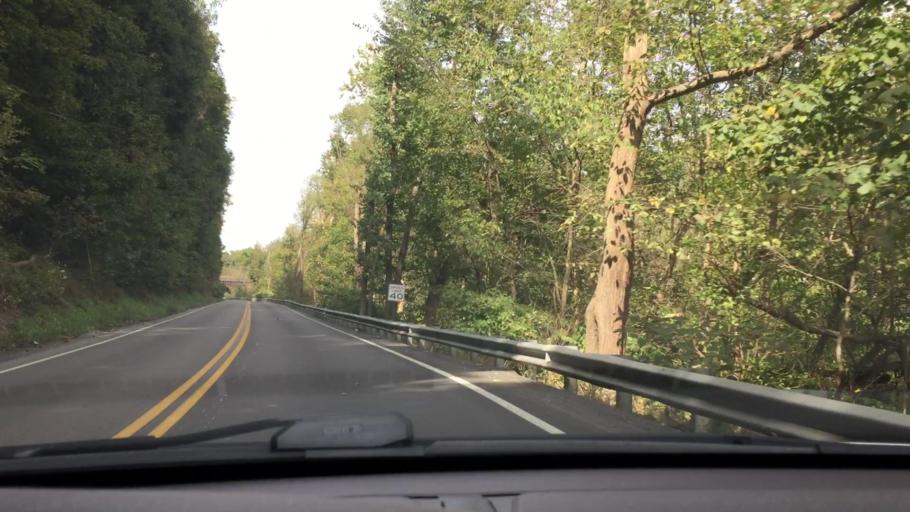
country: US
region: Pennsylvania
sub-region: Washington County
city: Thompsonville
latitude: 40.2987
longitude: -80.1093
